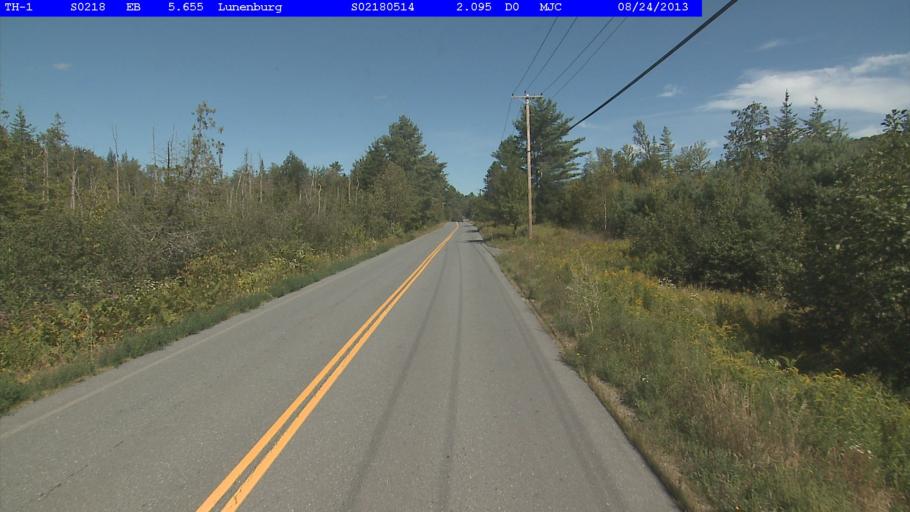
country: US
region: New Hampshire
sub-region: Coos County
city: Whitefield
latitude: 44.4142
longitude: -71.7127
